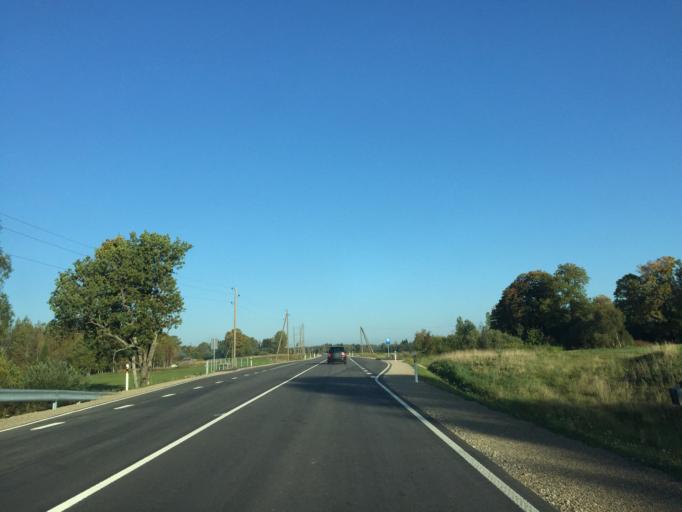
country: LV
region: Vecpiebalga
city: Vecpiebalga
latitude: 57.0915
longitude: 25.7369
